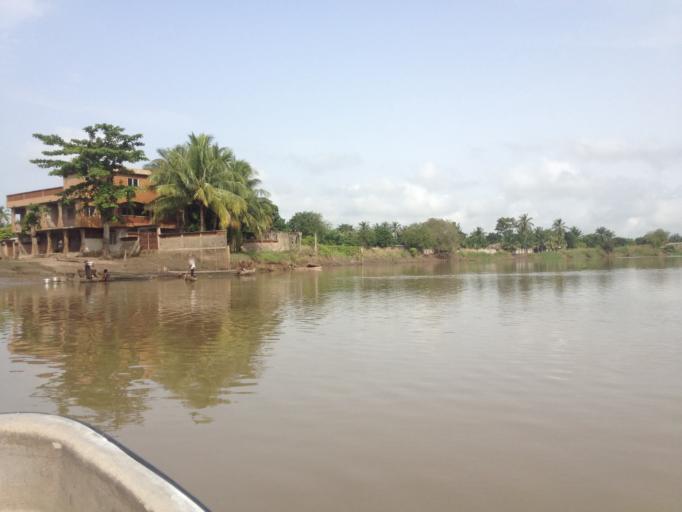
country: BJ
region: Mono
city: Grand-Popo
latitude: 6.3321
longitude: 1.7842
